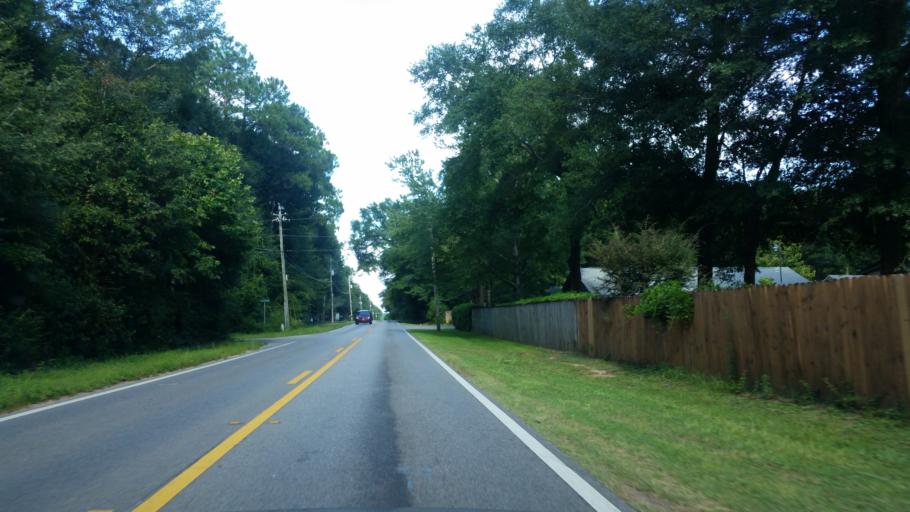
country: US
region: Florida
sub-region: Santa Rosa County
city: Pace
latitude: 30.6250
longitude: -87.1235
